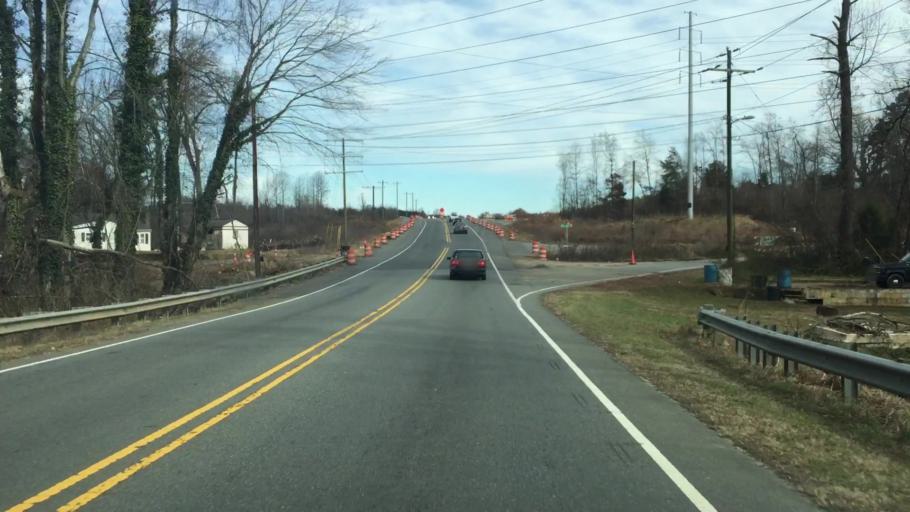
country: US
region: North Carolina
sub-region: Forsyth County
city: Walkertown
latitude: 36.1416
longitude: -80.1609
